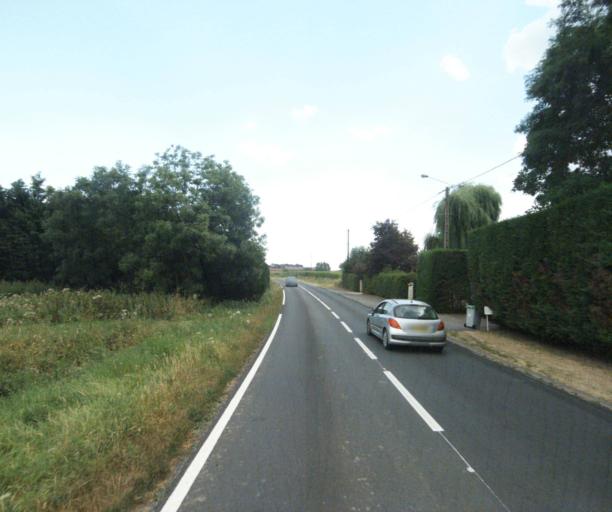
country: FR
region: Nord-Pas-de-Calais
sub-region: Departement du Nord
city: Quesnoy-sur-Deule
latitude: 50.7189
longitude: 2.9885
